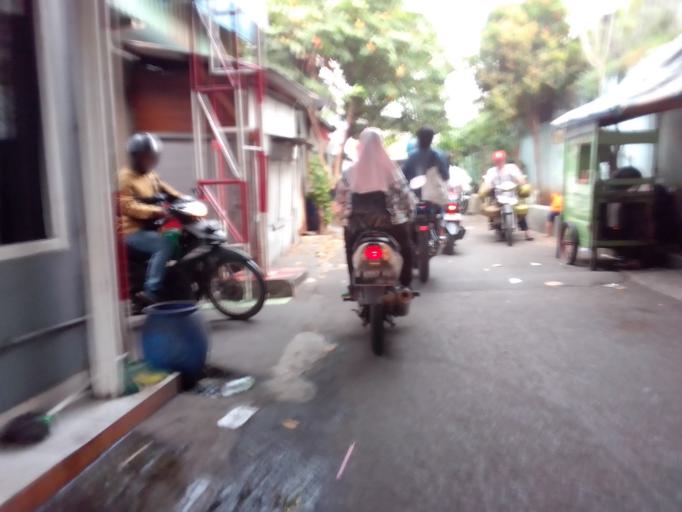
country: ID
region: Jakarta Raya
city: Jakarta
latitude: -6.1643
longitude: 106.7999
